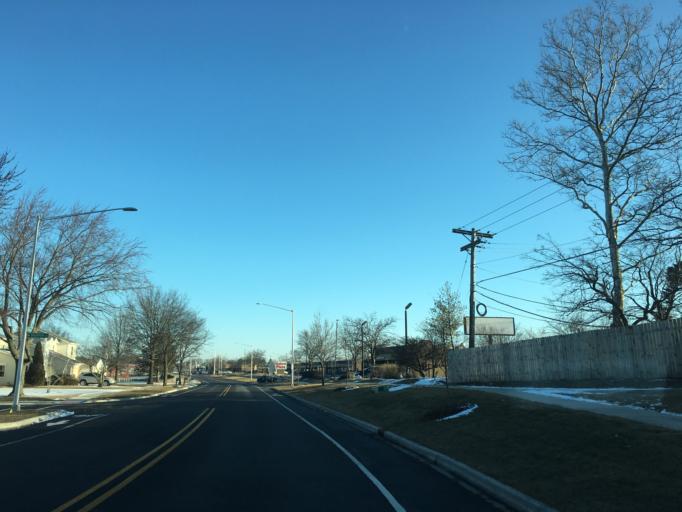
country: US
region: Illinois
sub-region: Cook County
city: Schaumburg
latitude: 42.0446
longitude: -88.0997
